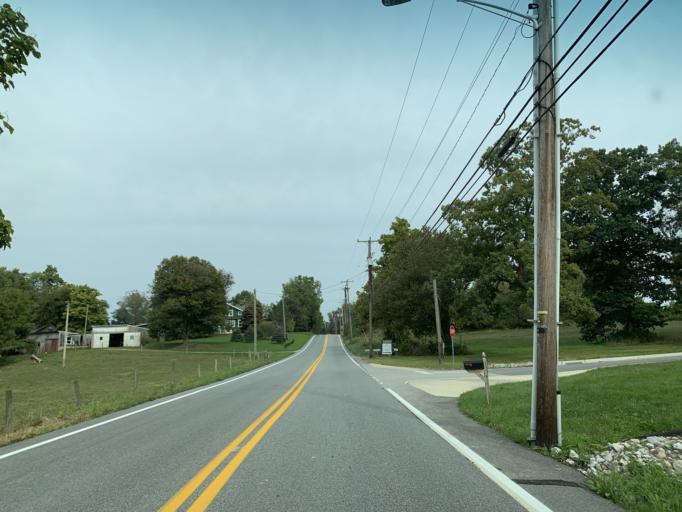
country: US
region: Pennsylvania
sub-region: York County
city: Susquehanna Trails
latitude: 39.7323
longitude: -76.4517
